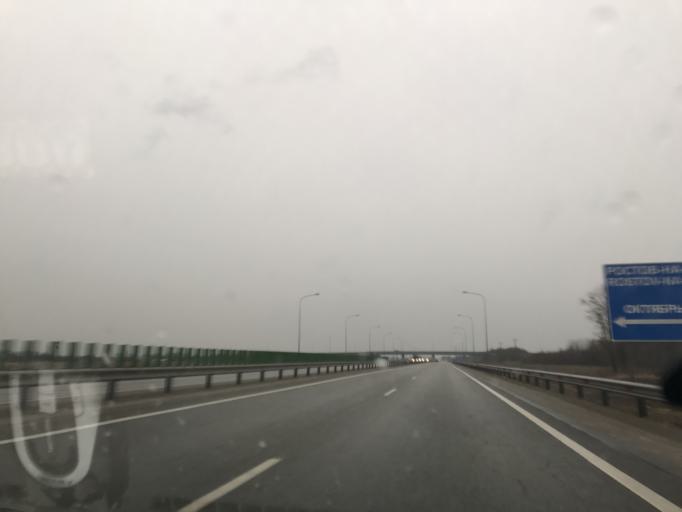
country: RU
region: Krasnodarskiy
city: Pavlovskaya
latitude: 46.2606
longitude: 39.8317
